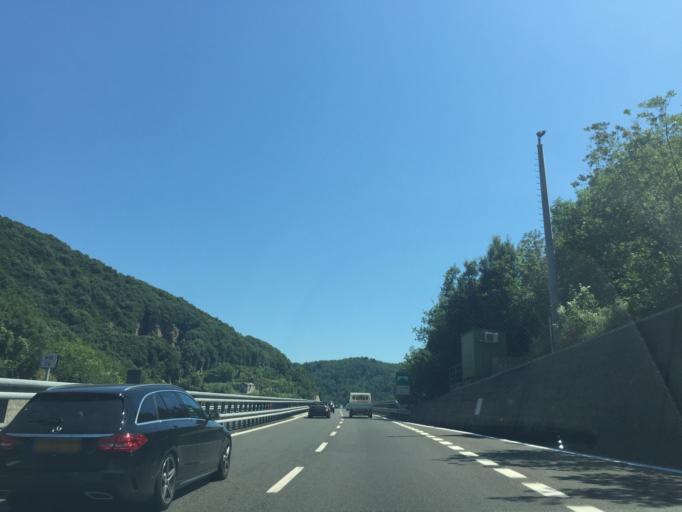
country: IT
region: Tuscany
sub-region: Provincia di Lucca
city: Massarosa
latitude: 43.8593
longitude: 10.3681
